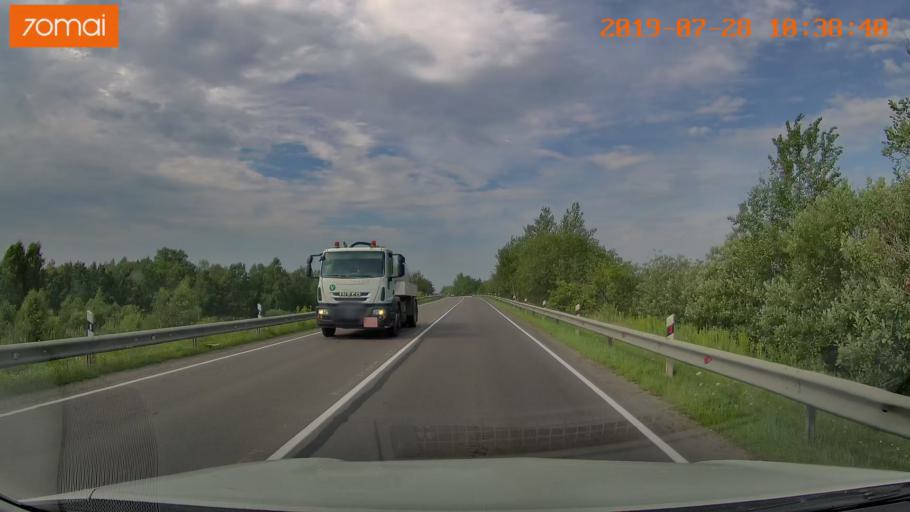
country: RU
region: Kaliningrad
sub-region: Gorod Kaliningrad
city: Kaliningrad
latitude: 54.7226
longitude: 20.3948
